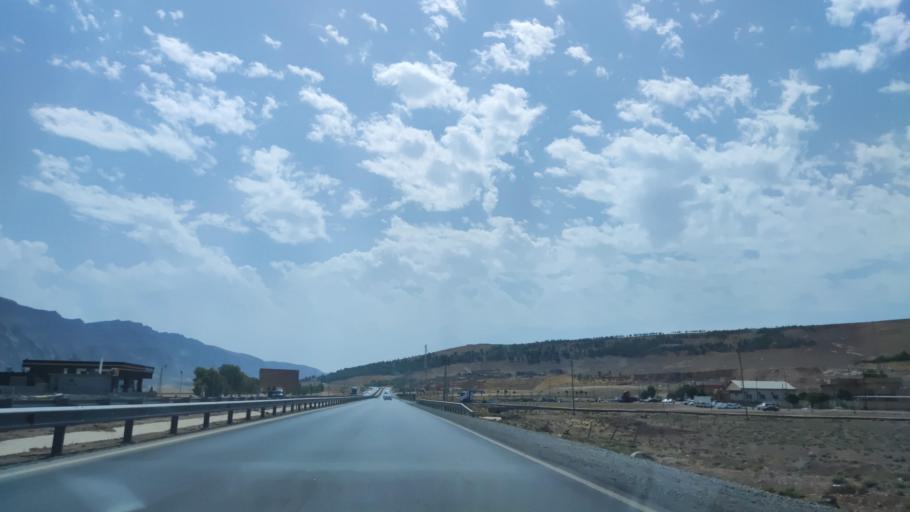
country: IQ
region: Arbil
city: Shaqlawah
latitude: 36.4998
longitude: 44.3595
